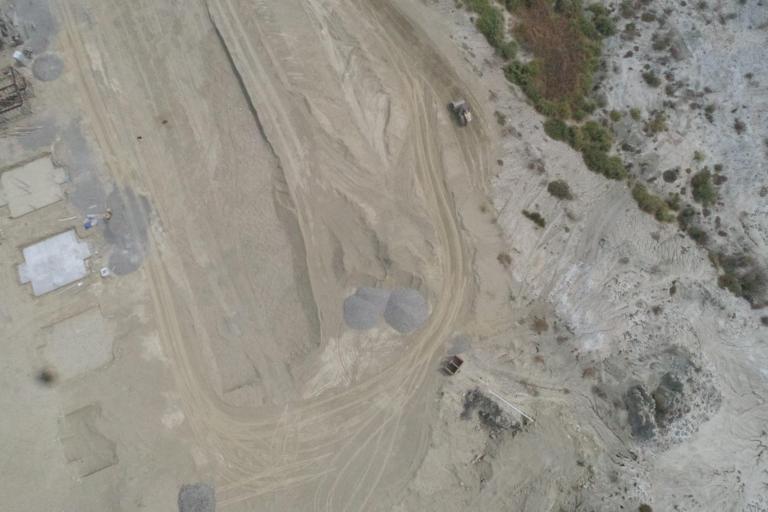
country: BO
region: La Paz
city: La Paz
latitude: -16.6017
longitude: -68.0677
